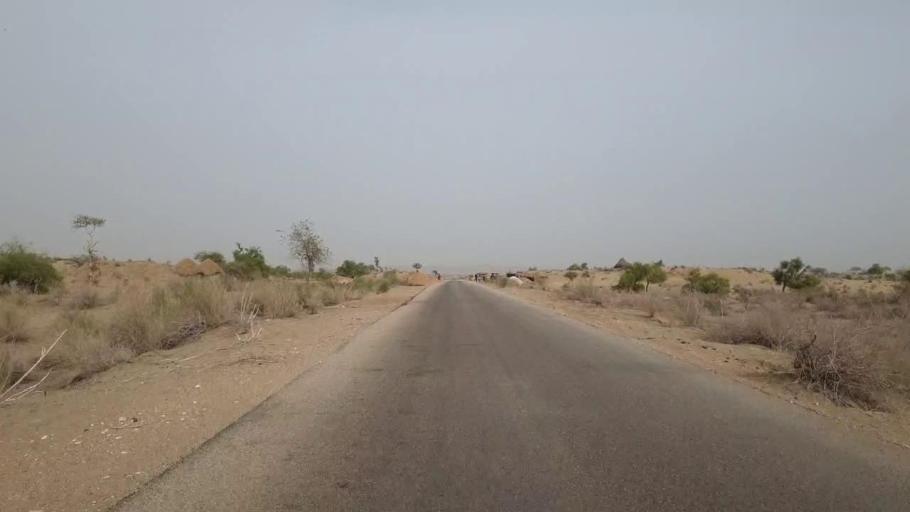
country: PK
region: Sindh
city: Islamkot
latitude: 24.5568
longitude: 70.3470
